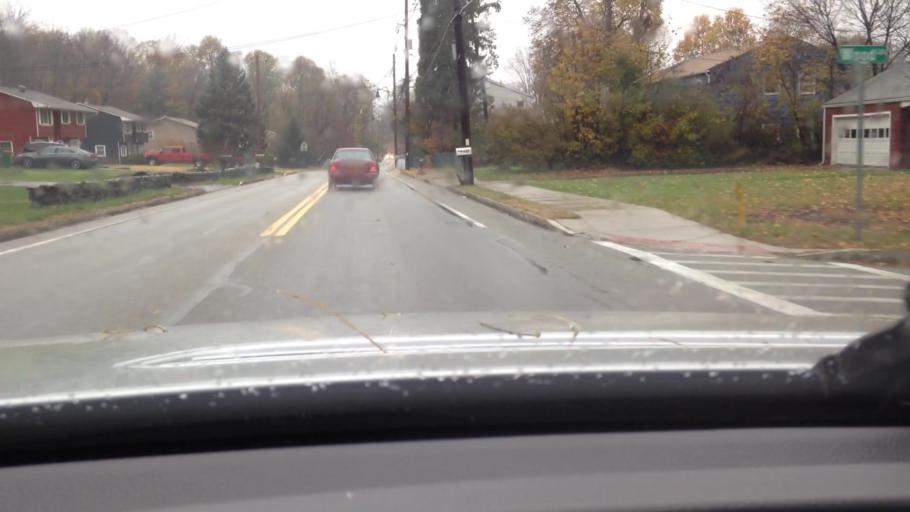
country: US
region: New York
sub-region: Dutchess County
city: Beacon
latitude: 41.4927
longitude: -73.9618
